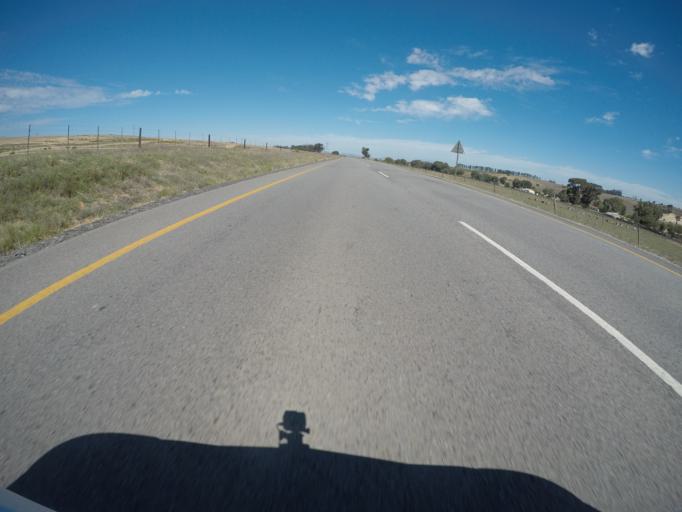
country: ZA
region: Western Cape
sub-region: West Coast District Municipality
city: Malmesbury
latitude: -33.4984
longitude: 18.6806
